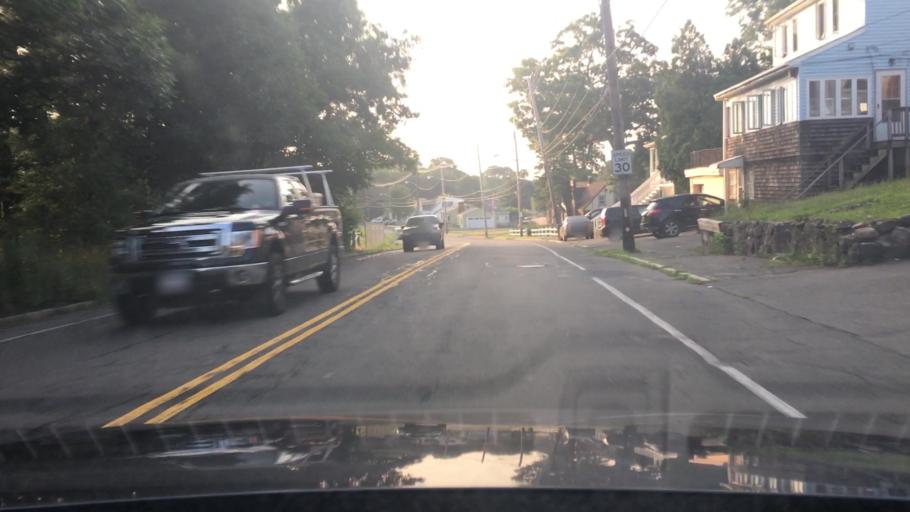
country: US
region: Massachusetts
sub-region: Essex County
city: Saugus
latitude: 42.4746
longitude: -70.9949
